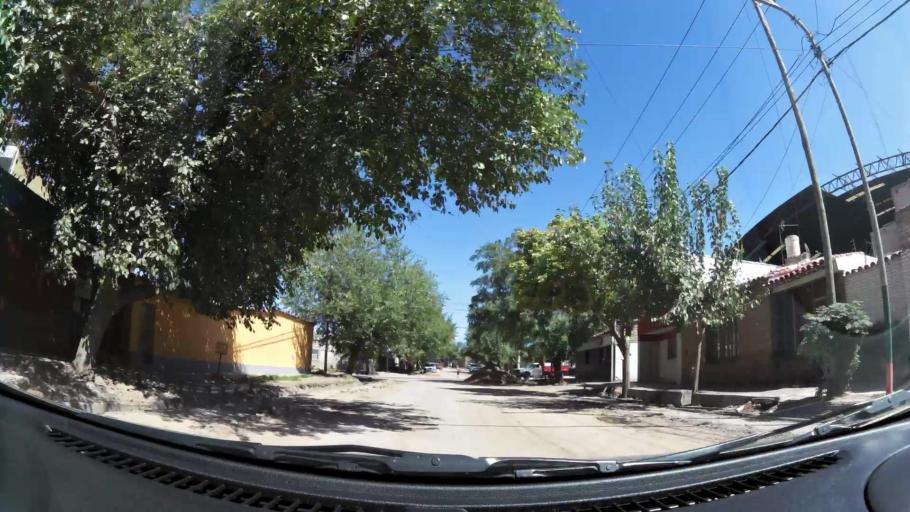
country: AR
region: Mendoza
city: Mendoza
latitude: -32.8803
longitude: -68.8210
